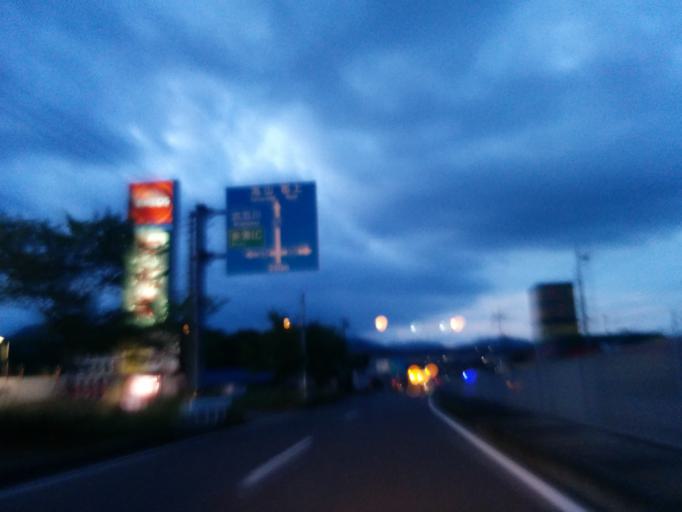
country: JP
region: Gifu
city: Mino
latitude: 35.5271
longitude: 136.9078
